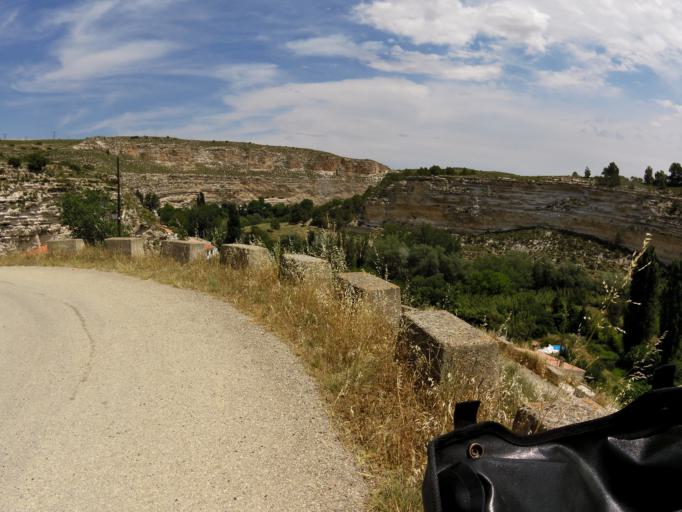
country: ES
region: Castille-La Mancha
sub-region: Provincia de Albacete
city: Valdeganga
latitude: 39.1607
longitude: -1.6096
